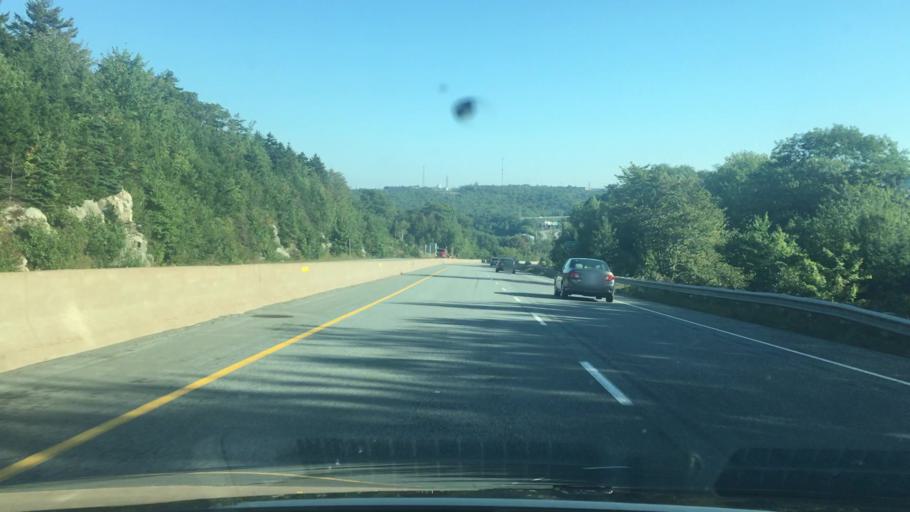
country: CA
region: Nova Scotia
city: Dartmouth
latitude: 44.7376
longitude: -63.6615
